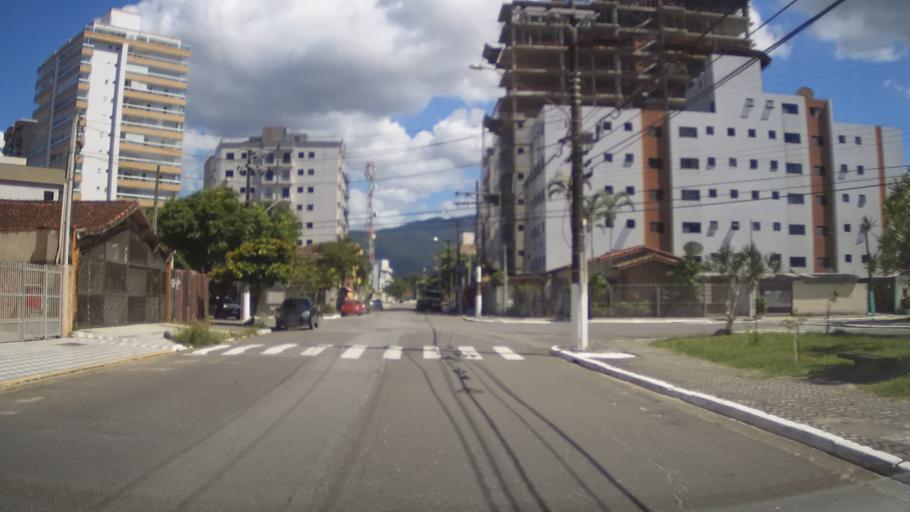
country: BR
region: Sao Paulo
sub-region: Mongagua
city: Mongagua
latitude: -24.0524
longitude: -46.5303
